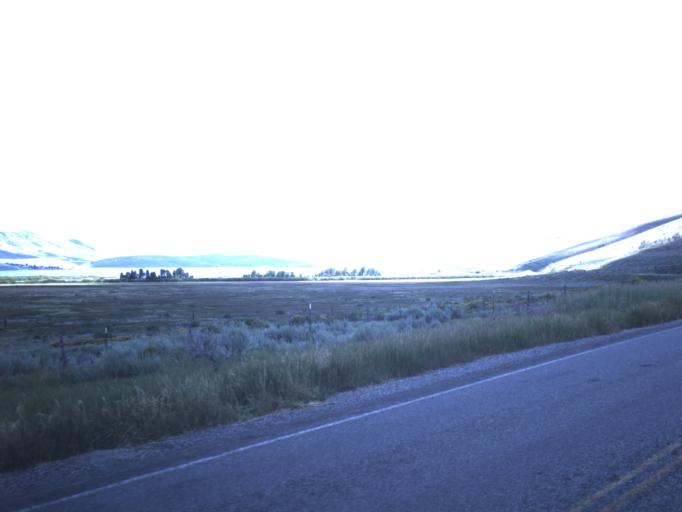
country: US
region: Utah
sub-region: Sanpete County
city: Fairview
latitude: 39.7310
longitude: -111.1565
